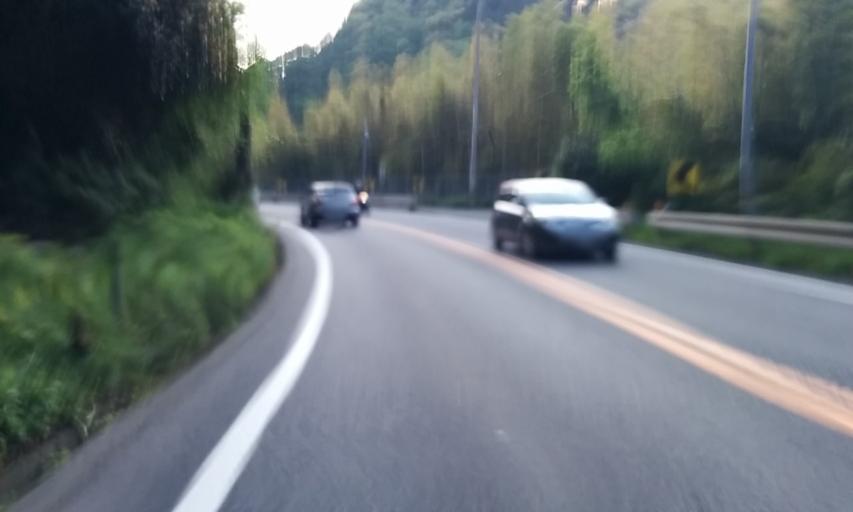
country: JP
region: Ehime
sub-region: Shikoku-chuo Shi
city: Matsuyama
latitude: 33.8242
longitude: 132.9837
